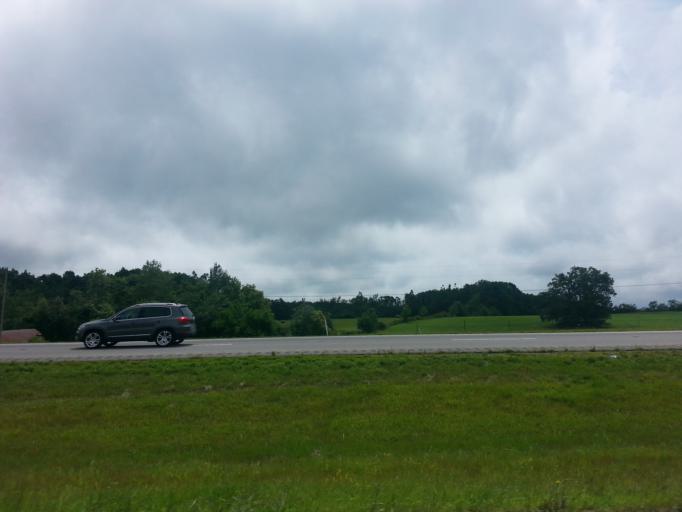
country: US
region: Tennessee
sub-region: Putnam County
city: Monterey
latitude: 36.1023
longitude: -85.2377
